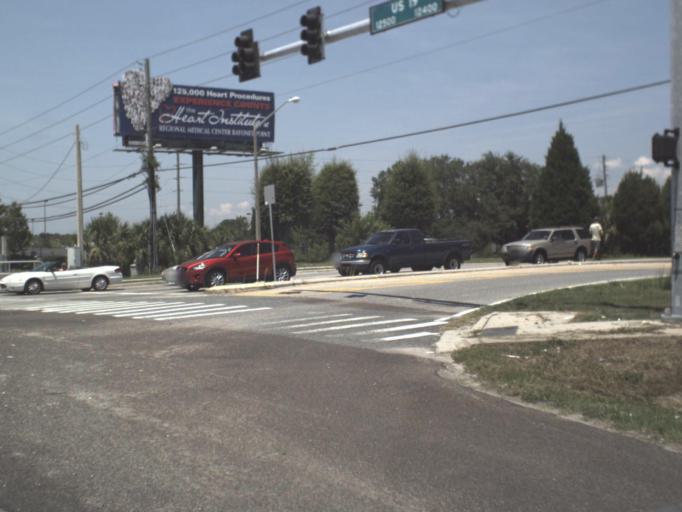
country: US
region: Florida
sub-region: Pasco County
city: Bayonet Point
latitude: 28.3382
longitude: -82.6991
